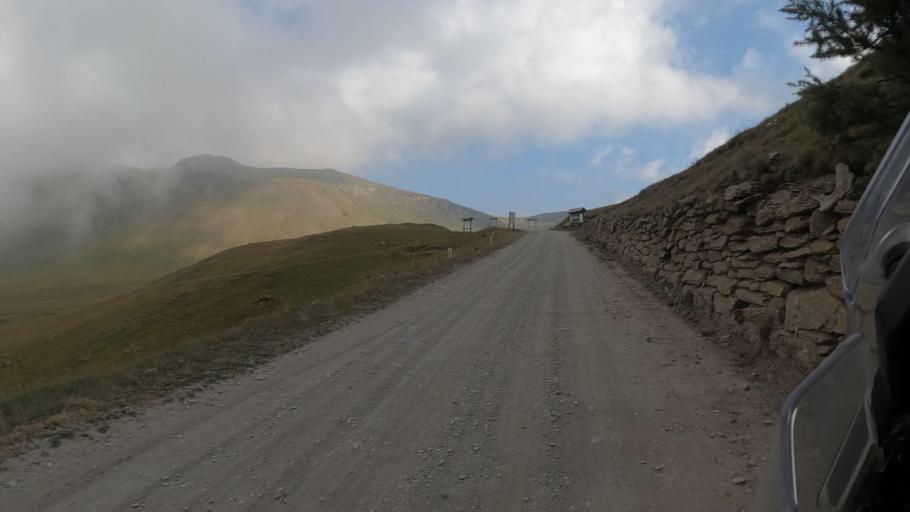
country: IT
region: Piedmont
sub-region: Provincia di Torino
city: Exilles
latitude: 45.0632
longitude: 6.9637
